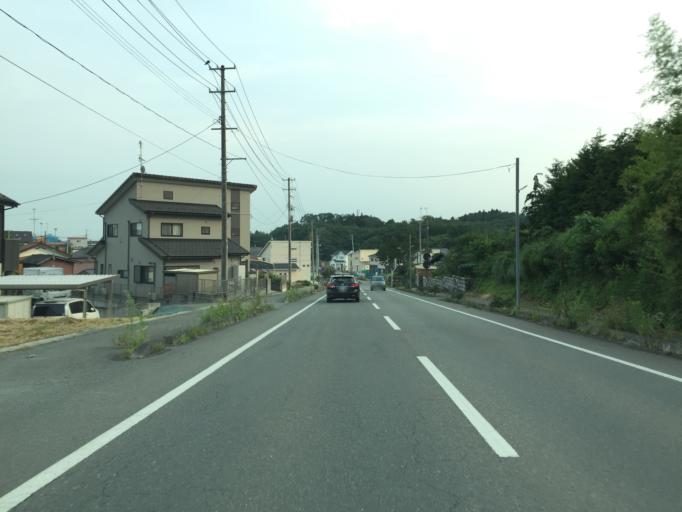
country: JP
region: Miyagi
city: Marumori
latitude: 37.7963
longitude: 140.9110
